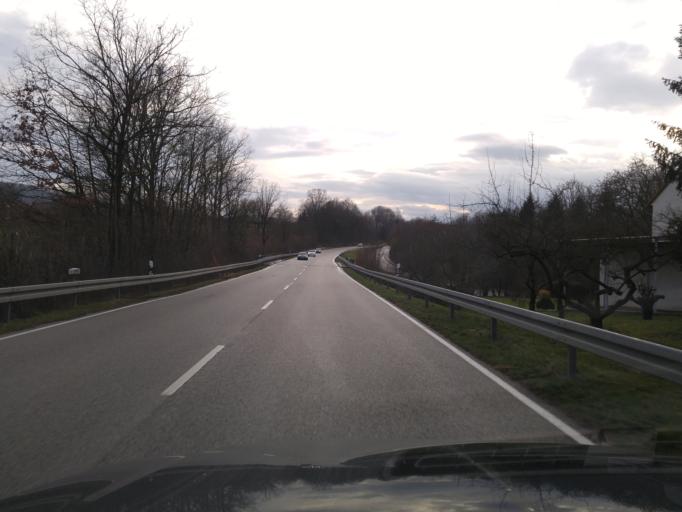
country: DE
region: Baden-Wuerttemberg
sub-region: Regierungsbezirk Stuttgart
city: Neuenstein
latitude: 49.2048
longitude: 9.5916
